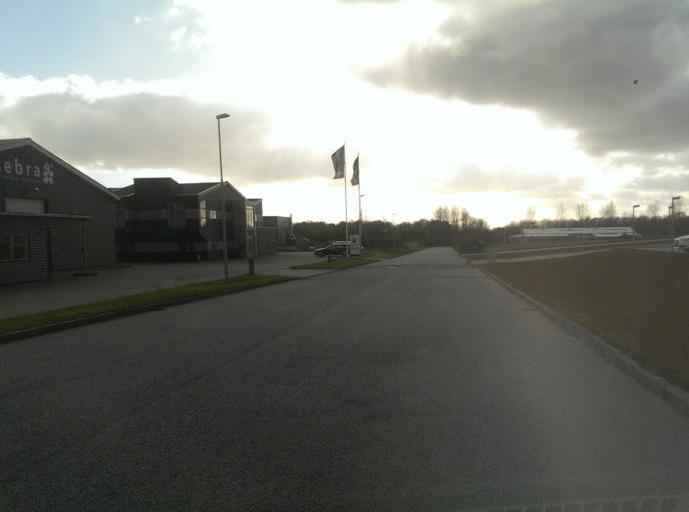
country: DK
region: South Denmark
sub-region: Esbjerg Kommune
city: Esbjerg
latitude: 55.5125
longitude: 8.4634
